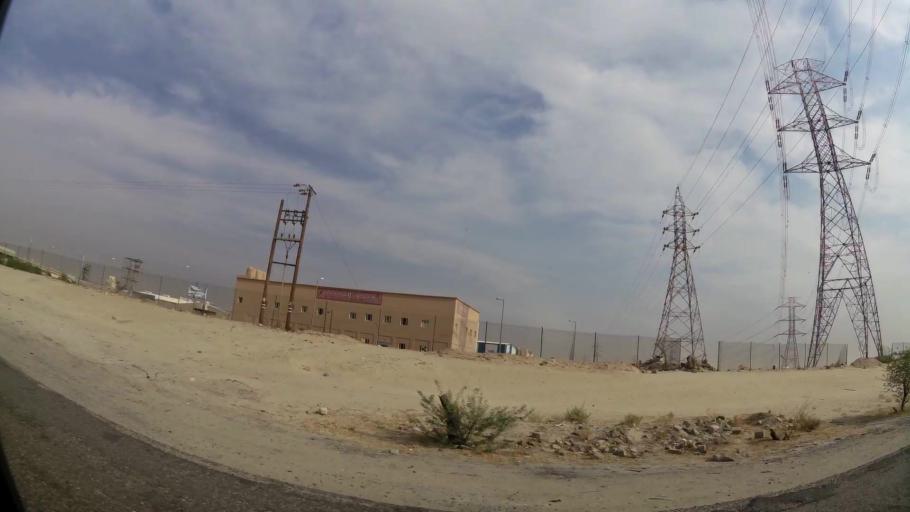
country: KW
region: Muhafazat al Jahra'
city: Al Jahra'
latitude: 29.2936
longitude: 47.7479
